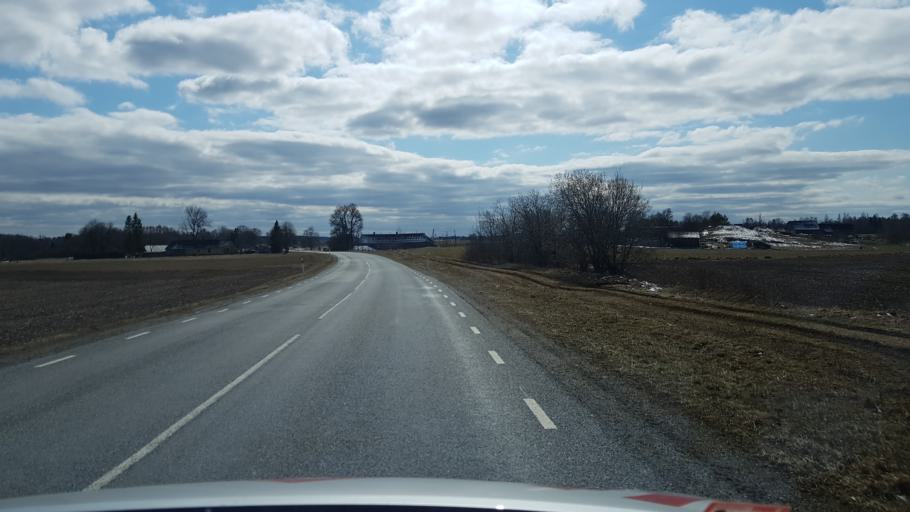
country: EE
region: Laeaene-Virumaa
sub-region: Tapa vald
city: Tapa
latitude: 59.3300
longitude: 26.0003
